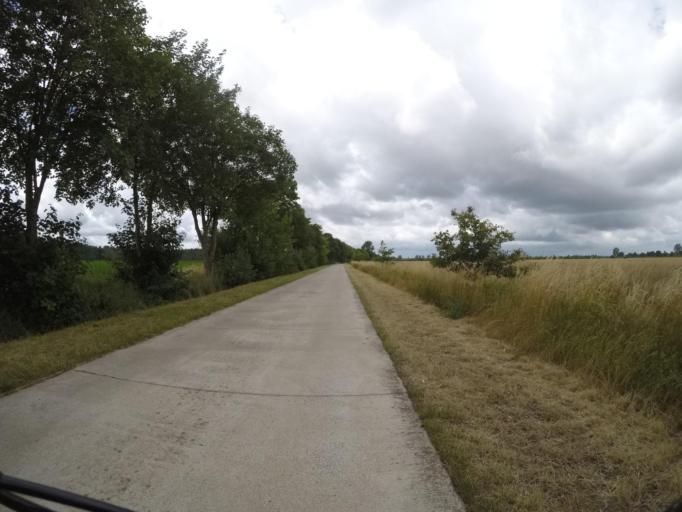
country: DE
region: Lower Saxony
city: Damnatz
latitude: 53.1949
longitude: 11.1183
